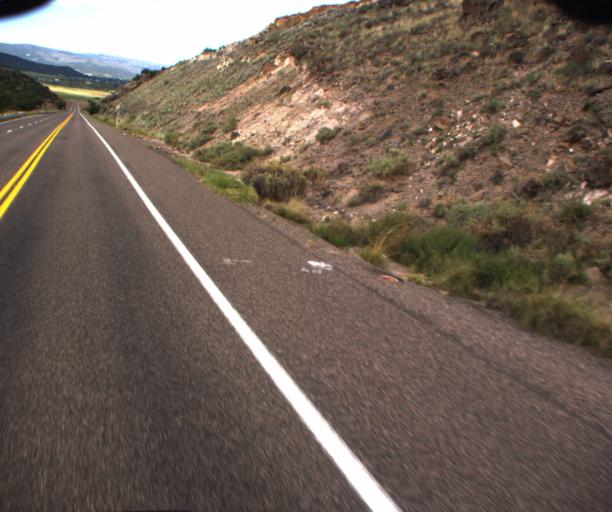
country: US
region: Arizona
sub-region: Apache County
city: Springerville
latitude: 34.1416
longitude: -109.2271
